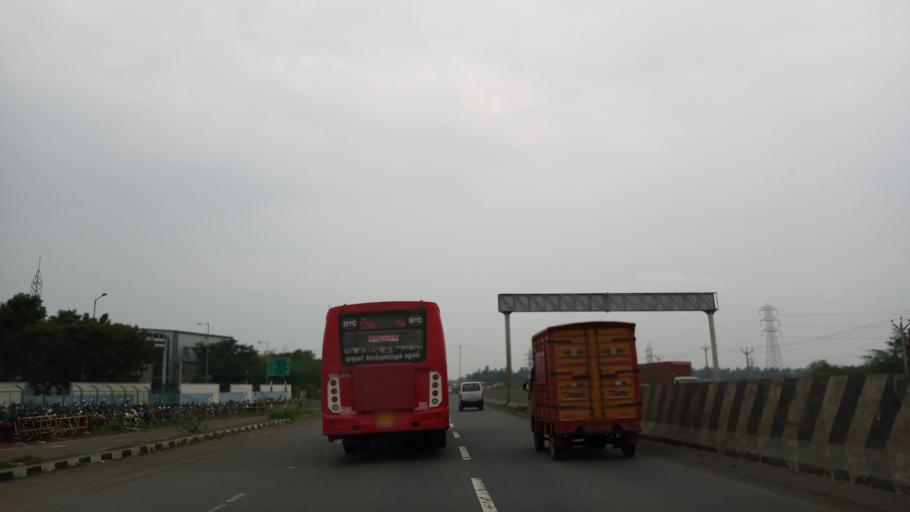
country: IN
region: Tamil Nadu
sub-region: Kancheepuram
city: Madambakkam
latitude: 12.8536
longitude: 79.9469
